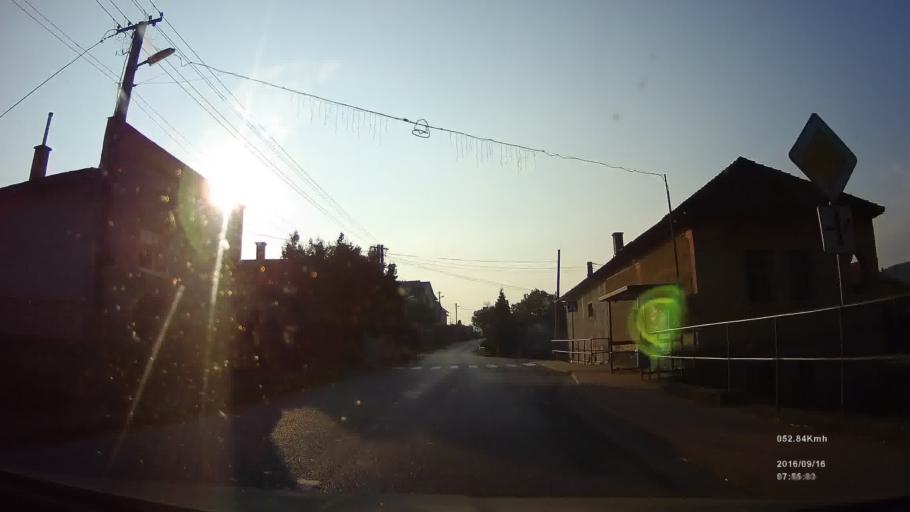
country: SK
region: Presovsky
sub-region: Okres Presov
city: Presov
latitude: 48.9161
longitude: 21.1225
